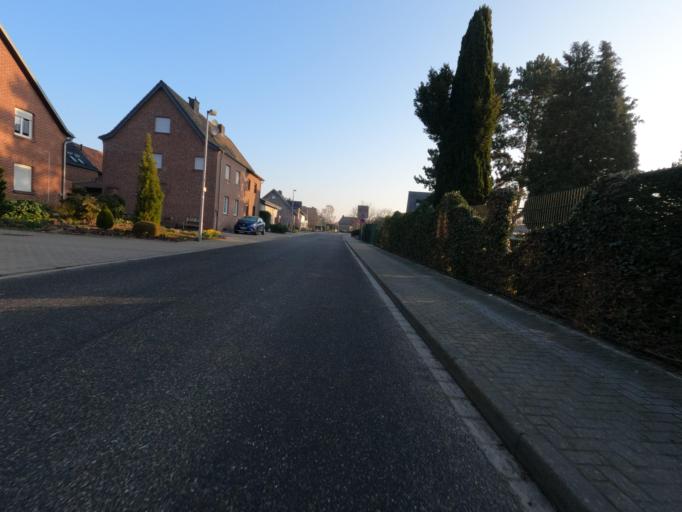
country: DE
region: North Rhine-Westphalia
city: Huckelhoven
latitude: 51.0700
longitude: 6.2477
